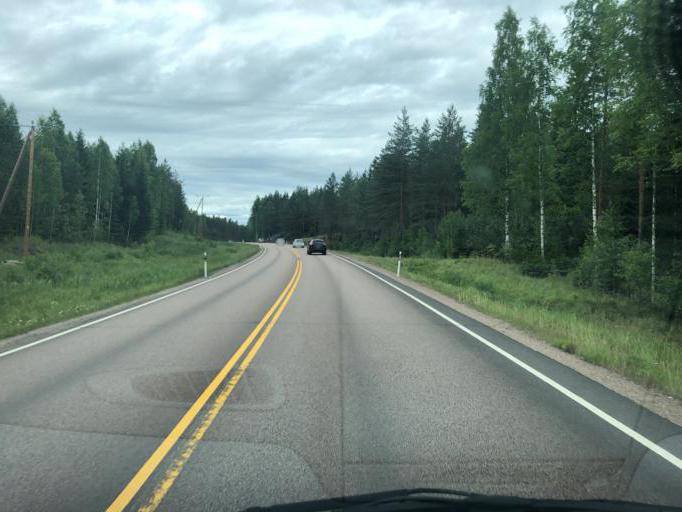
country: FI
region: Southern Savonia
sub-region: Mikkeli
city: Ristiina
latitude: 61.1652
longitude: 27.1479
